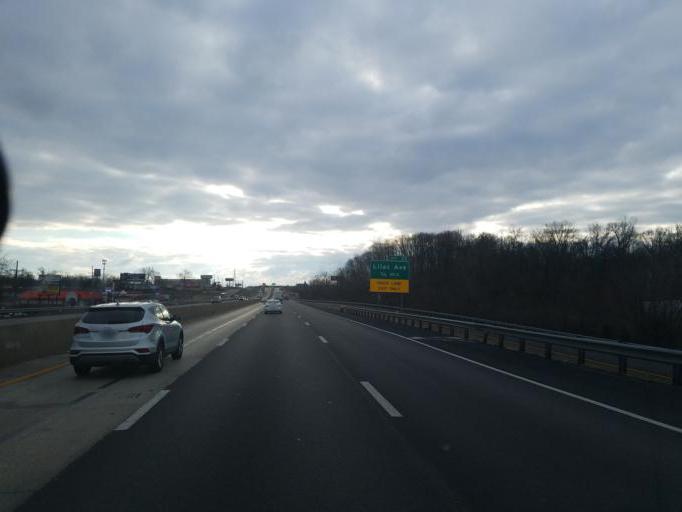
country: US
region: Missouri
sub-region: Saint Louis County
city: Spanish Lake
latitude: 38.7697
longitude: -90.2203
